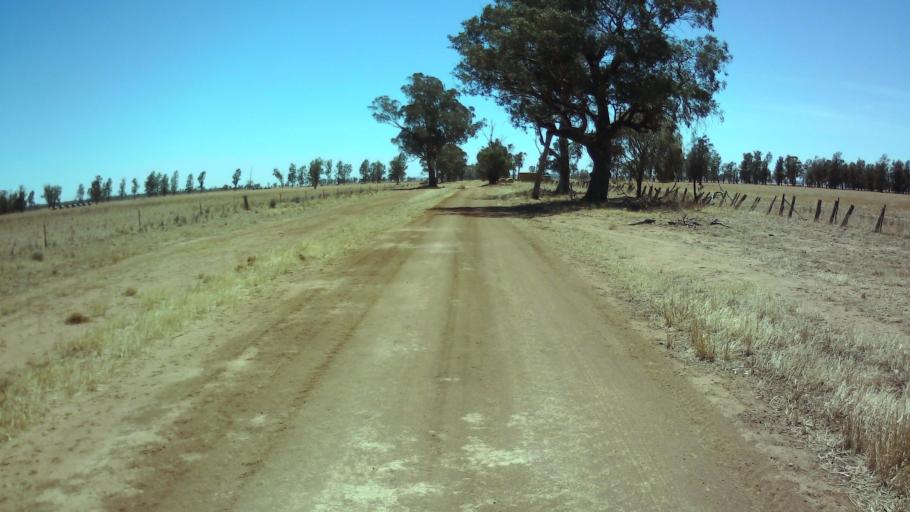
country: AU
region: New South Wales
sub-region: Weddin
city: Grenfell
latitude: -33.9718
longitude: 147.7379
